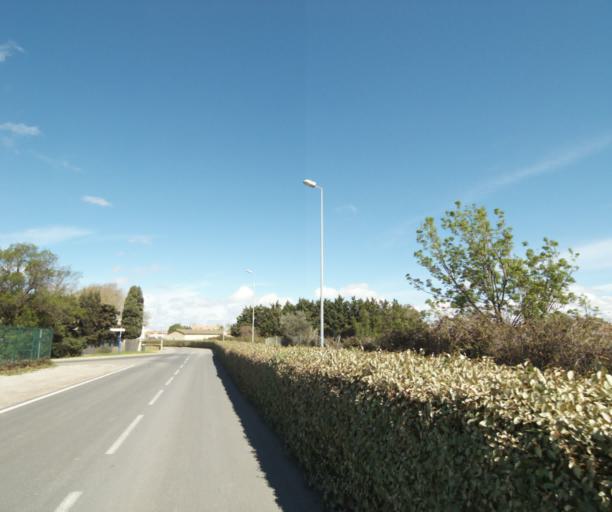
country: FR
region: Languedoc-Roussillon
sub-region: Departement de l'Herault
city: Villeneuve-les-Maguelone
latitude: 43.5311
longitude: 3.8659
